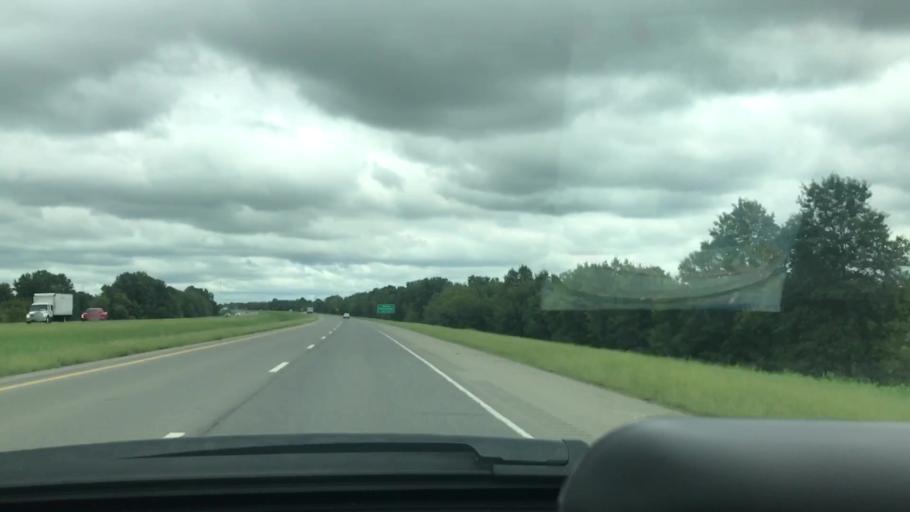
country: US
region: Oklahoma
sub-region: McIntosh County
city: Checotah
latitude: 35.5579
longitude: -95.4949
